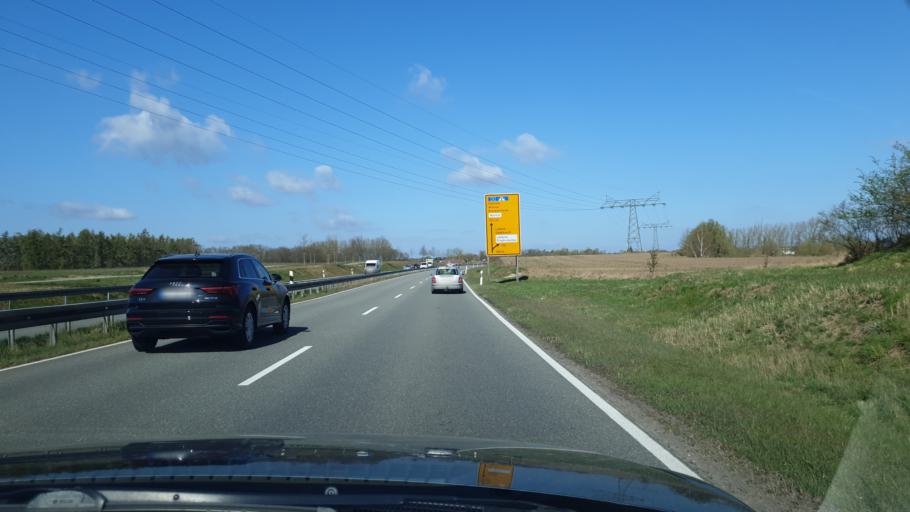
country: DE
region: Mecklenburg-Vorpommern
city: Lankow
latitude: 53.6408
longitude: 11.3505
